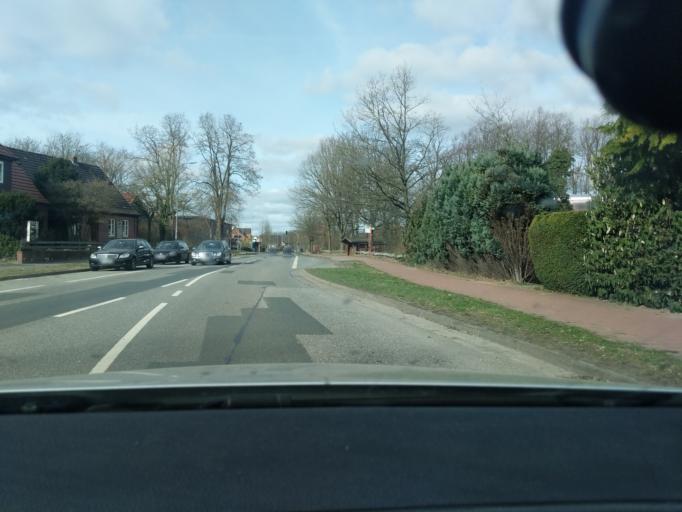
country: DE
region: Lower Saxony
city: Agathenburg
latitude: 53.5621
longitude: 9.5305
